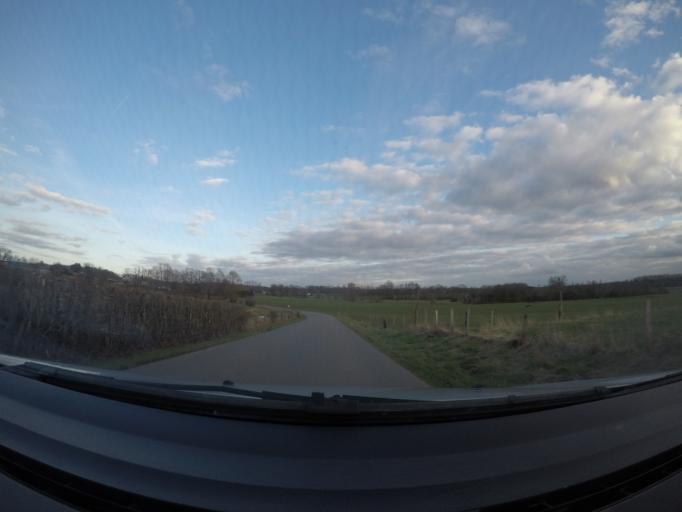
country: BE
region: Wallonia
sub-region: Province du Luxembourg
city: Tintigny
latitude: 49.7000
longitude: 5.5502
